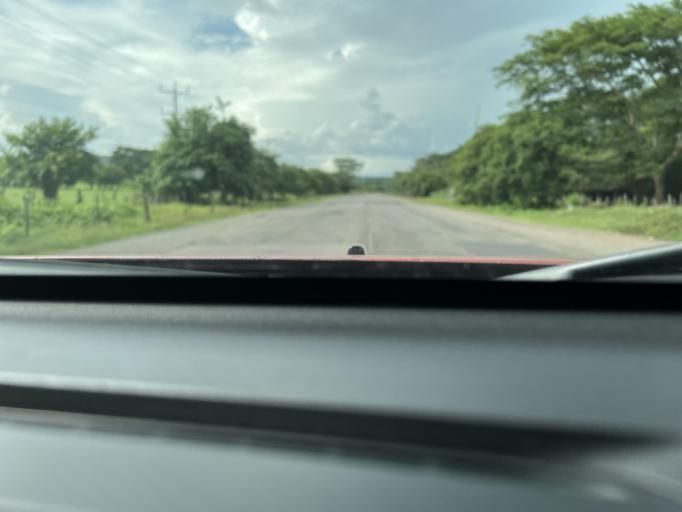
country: SV
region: La Union
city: La Union
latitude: 13.3745
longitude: -87.9091
